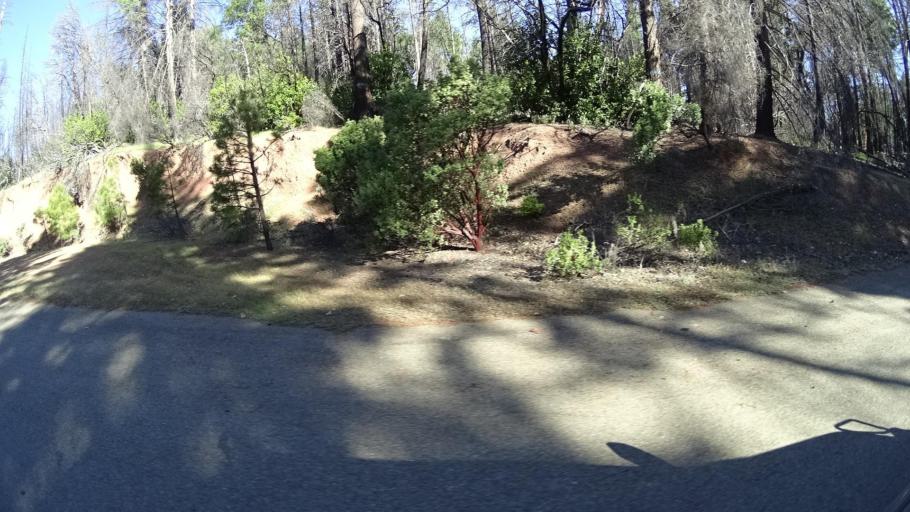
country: US
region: California
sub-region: Lake County
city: Upper Lake
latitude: 39.3970
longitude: -122.9678
